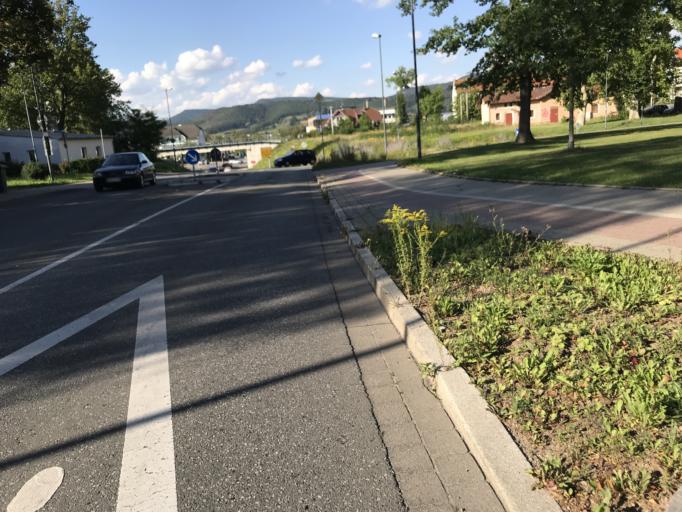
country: DE
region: Hesse
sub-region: Regierungsbezirk Kassel
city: Eschwege
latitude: 51.1908
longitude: 10.0391
